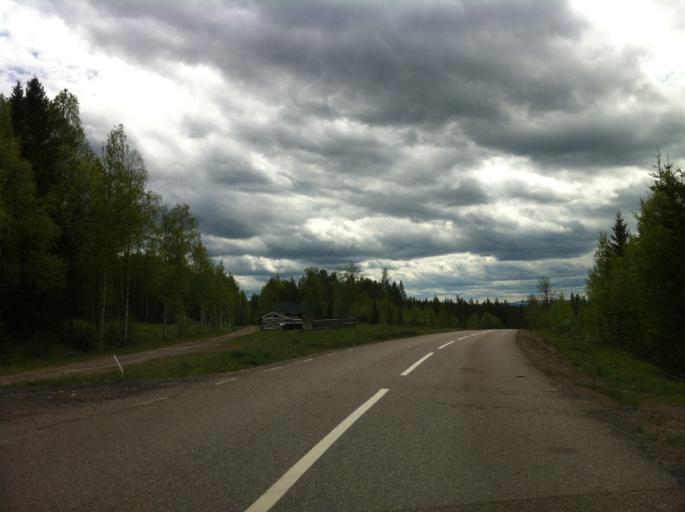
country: NO
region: Hedmark
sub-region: Trysil
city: Innbygda
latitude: 61.5157
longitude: 13.0840
